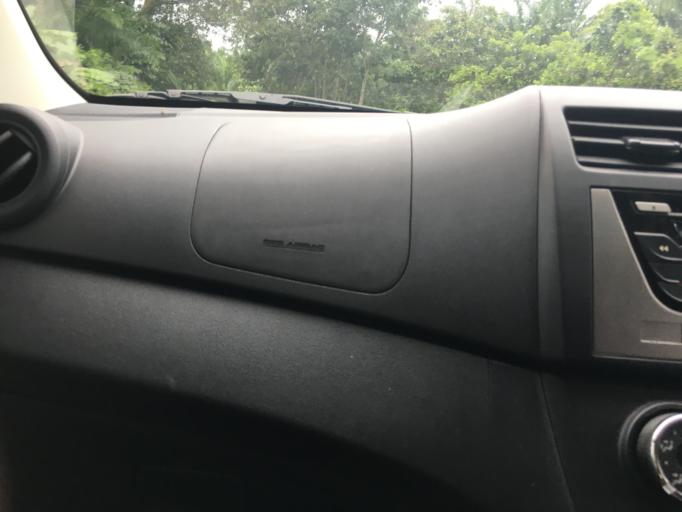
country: MY
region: Kedah
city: Bedong
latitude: 5.7111
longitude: 100.6312
